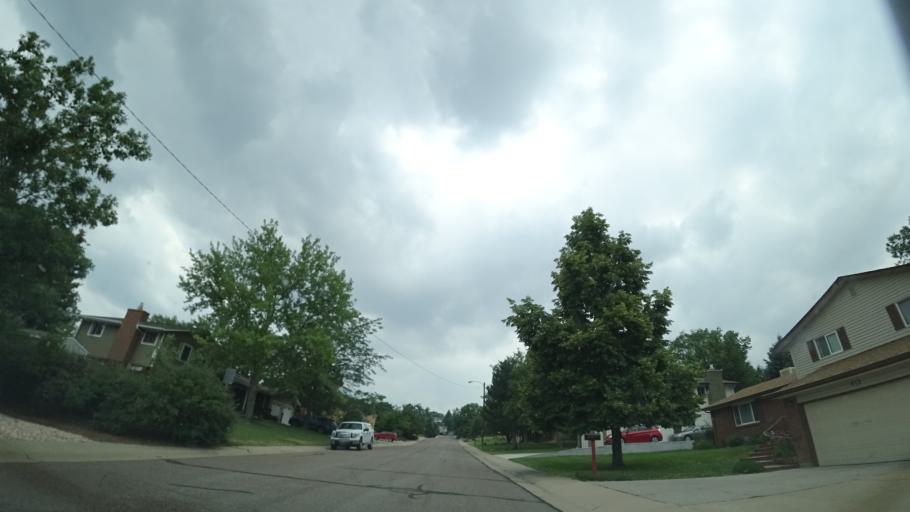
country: US
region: Colorado
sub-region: Jefferson County
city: West Pleasant View
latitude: 39.7094
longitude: -105.1555
